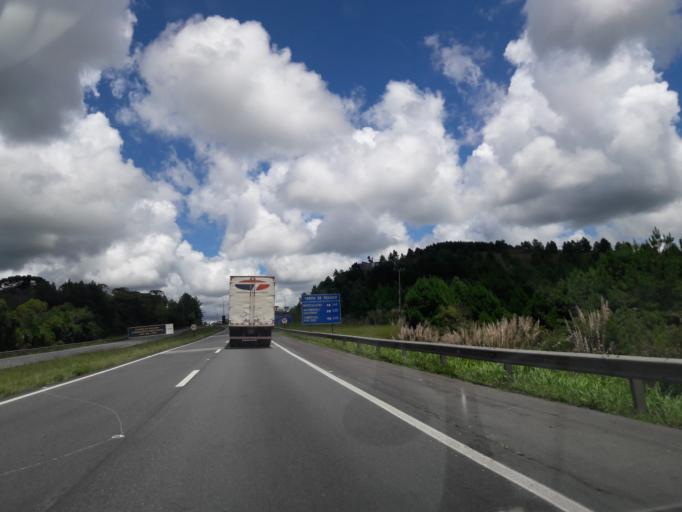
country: BR
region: Parana
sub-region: Campina Grande Do Sul
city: Campina Grande do Sul
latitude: -25.2854
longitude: -48.9307
